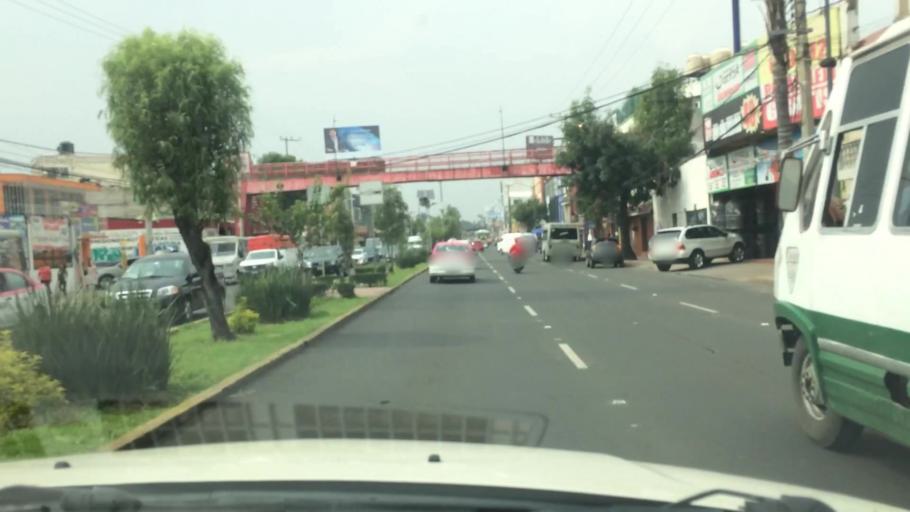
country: MX
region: Mexico City
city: Xochimilco
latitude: 19.2763
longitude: -99.1213
